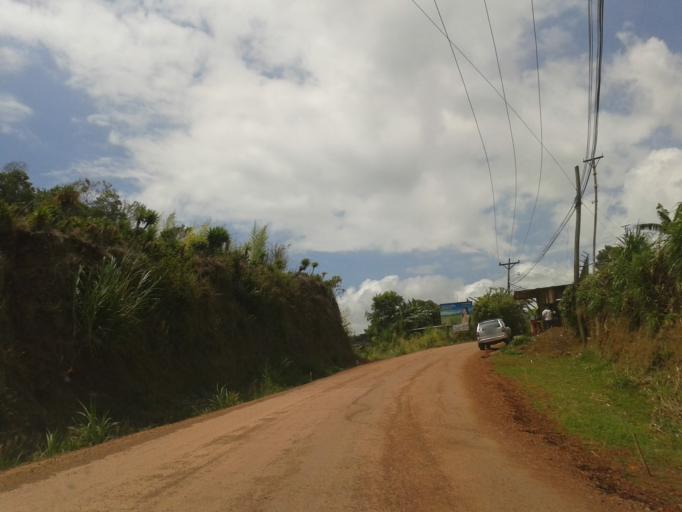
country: CR
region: Alajuela
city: Sabanilla
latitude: 10.0856
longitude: -84.1905
